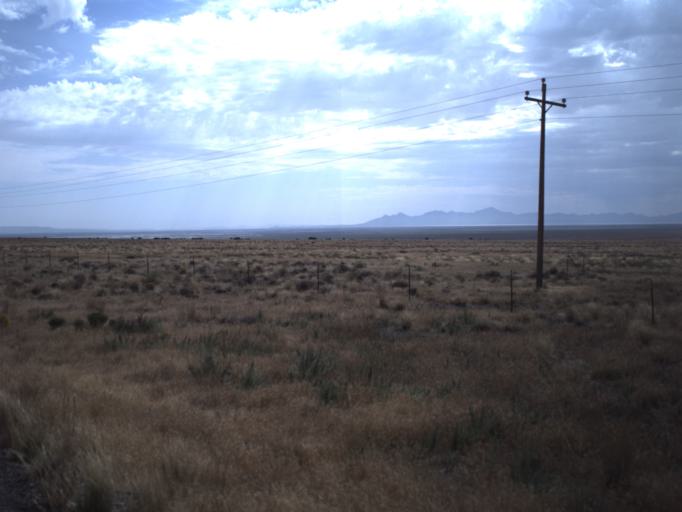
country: US
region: Utah
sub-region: Tooele County
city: Wendover
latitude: 41.4333
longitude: -113.7770
